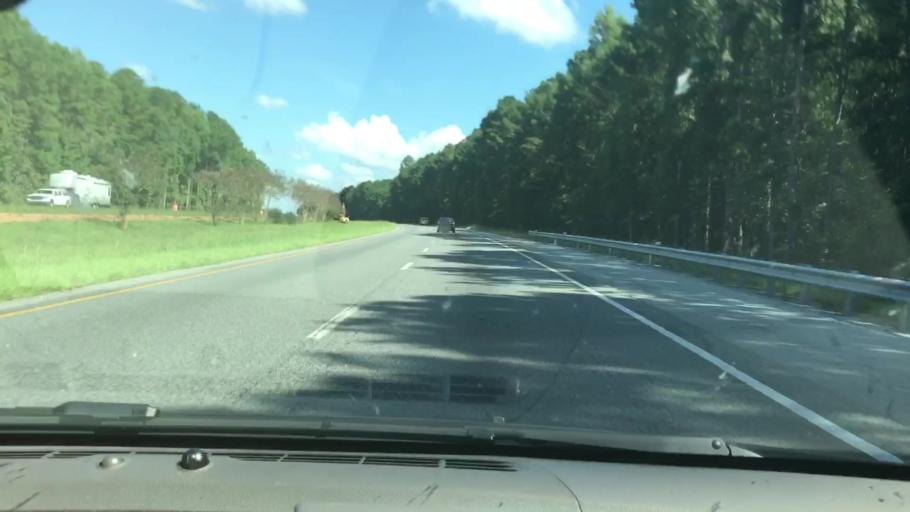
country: US
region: Georgia
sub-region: Harris County
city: Hamilton
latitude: 32.7291
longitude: -85.0183
